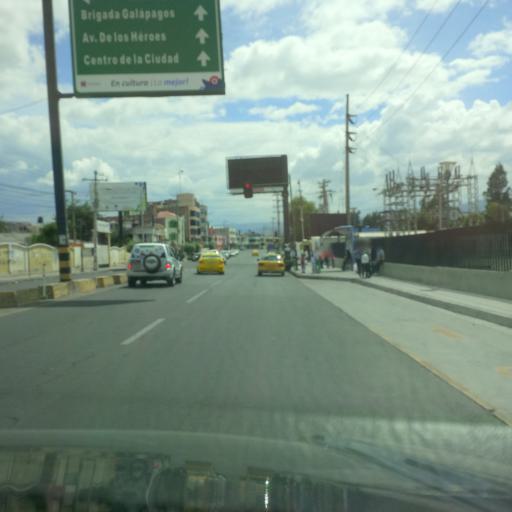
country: EC
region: Chimborazo
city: Riobamba
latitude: -1.6550
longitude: -78.6451
